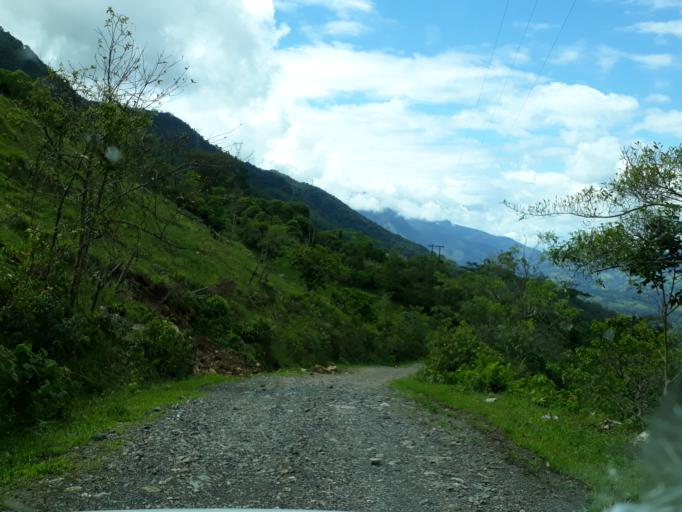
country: CO
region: Cundinamarca
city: Gachala
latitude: 4.7141
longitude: -73.3630
